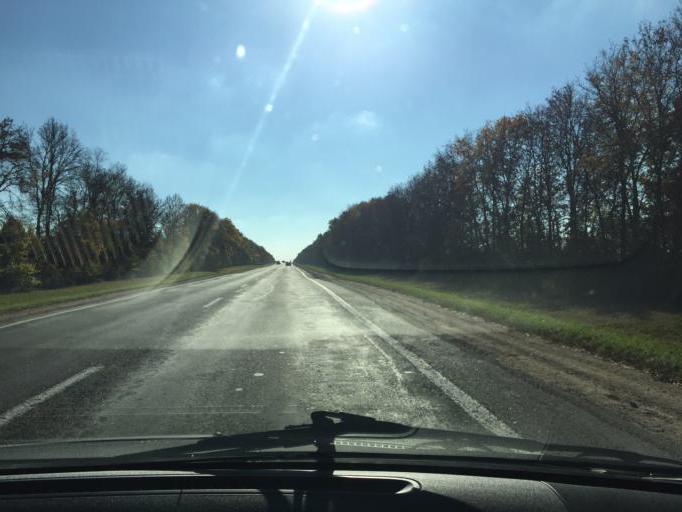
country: BY
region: Minsk
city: Slutsk
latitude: 52.9689
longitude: 27.5002
